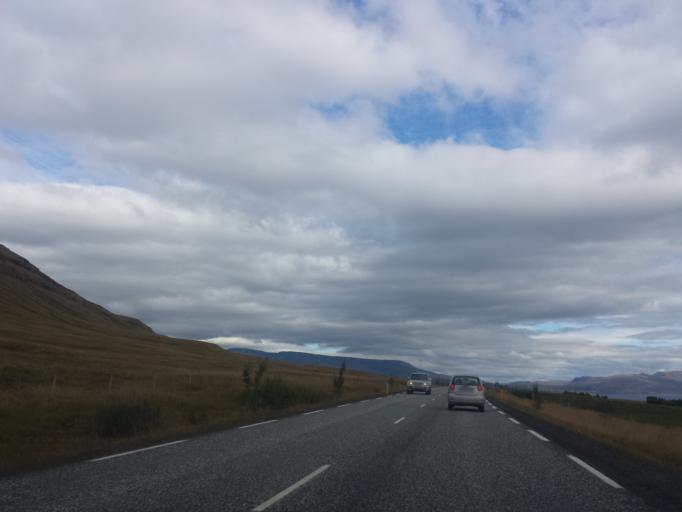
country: IS
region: Capital Region
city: Reykjavik
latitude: 64.3339
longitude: -21.8411
